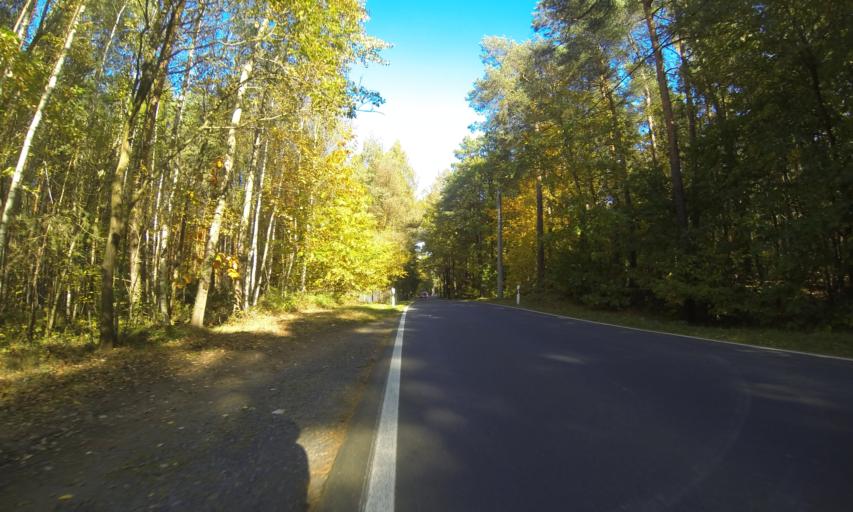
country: DE
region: Saxony
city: Weinbohla
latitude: 51.1875
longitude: 13.6071
